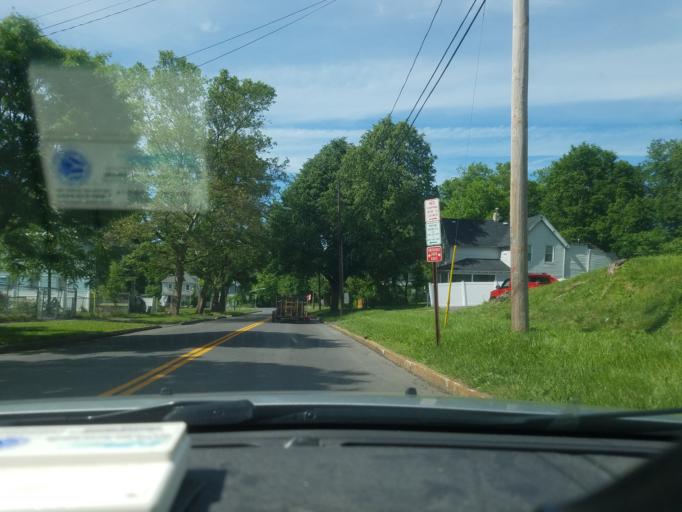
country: US
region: New York
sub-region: Onondaga County
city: Syracuse
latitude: 43.0472
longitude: -76.1198
